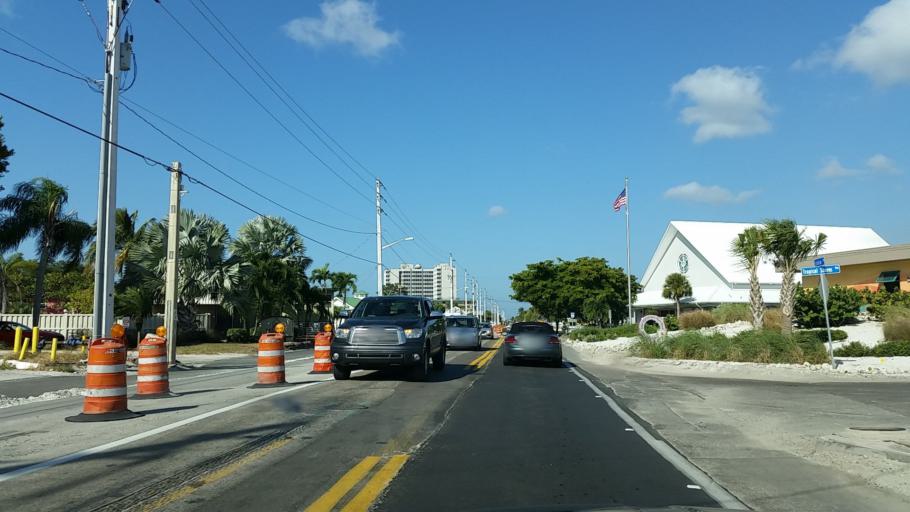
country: US
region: Florida
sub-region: Lee County
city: Fort Myers Beach
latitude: 26.4485
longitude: -81.9420
